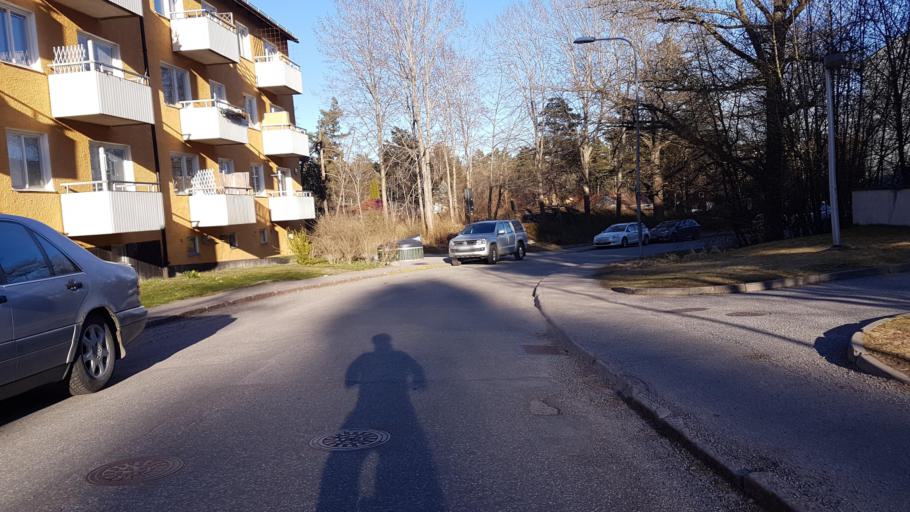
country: SE
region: Stockholm
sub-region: Stockholms Kommun
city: Arsta
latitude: 59.2662
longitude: 18.0778
